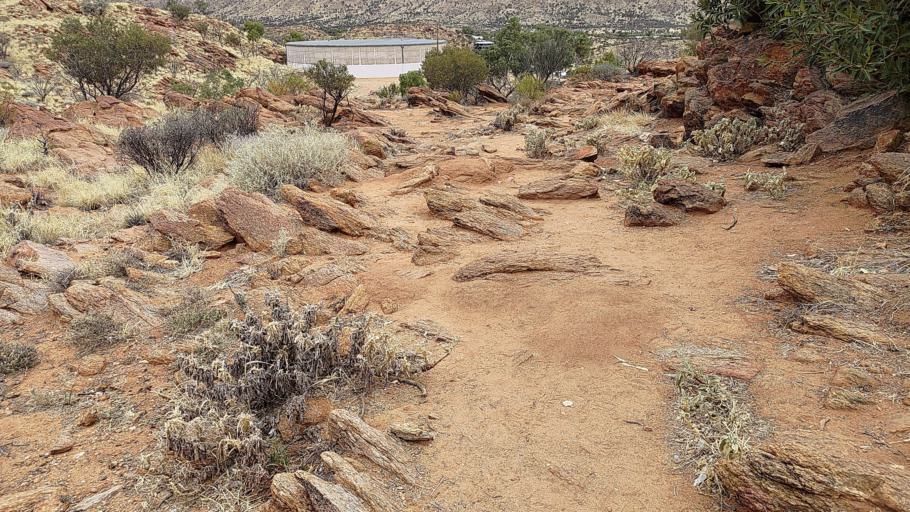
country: AU
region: Northern Territory
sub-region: Alice Springs
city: Alice Springs
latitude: -23.7052
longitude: 133.8864
